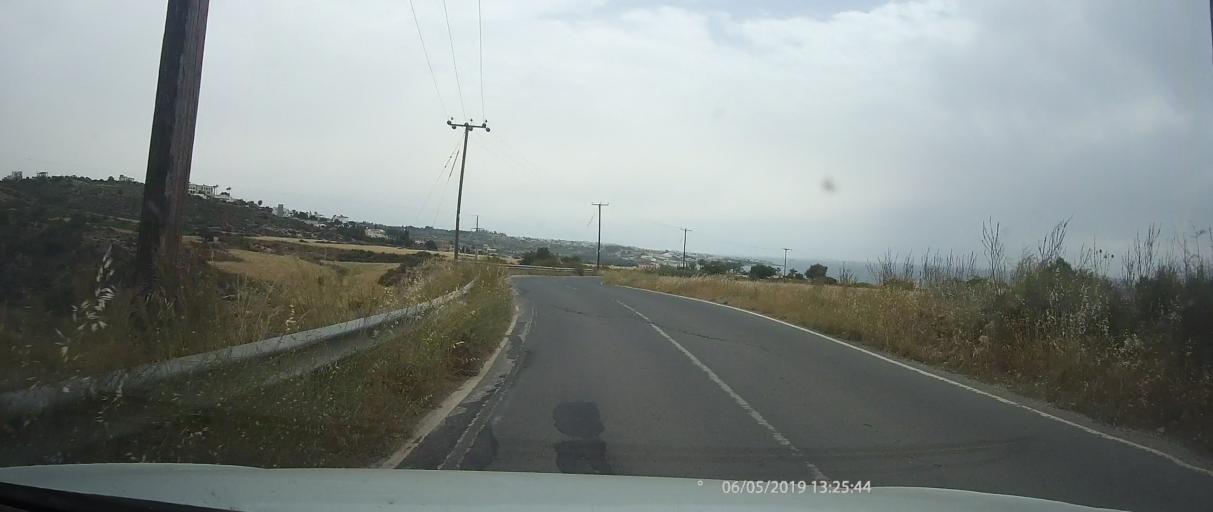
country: CY
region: Pafos
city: Pegeia
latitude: 34.8553
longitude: 32.3862
